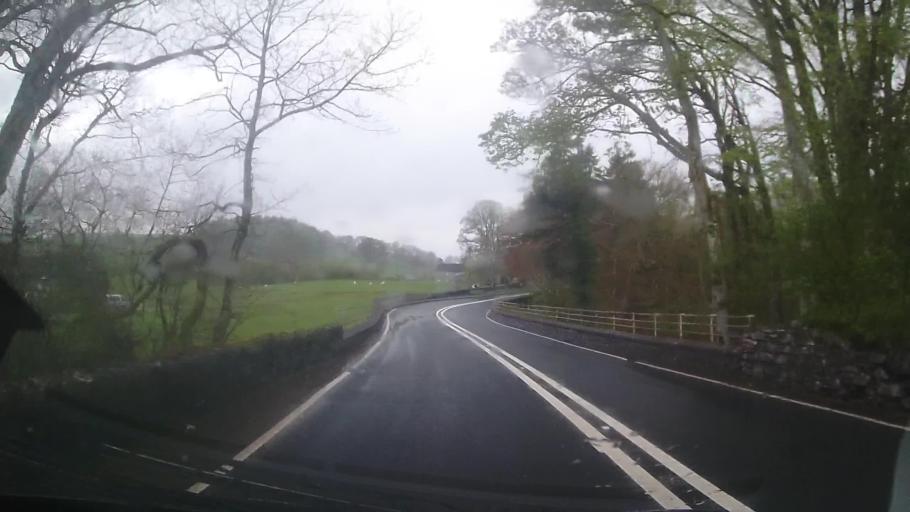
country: GB
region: Wales
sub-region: Conwy
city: Betws-y-Coed
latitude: 53.0455
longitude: -3.7073
